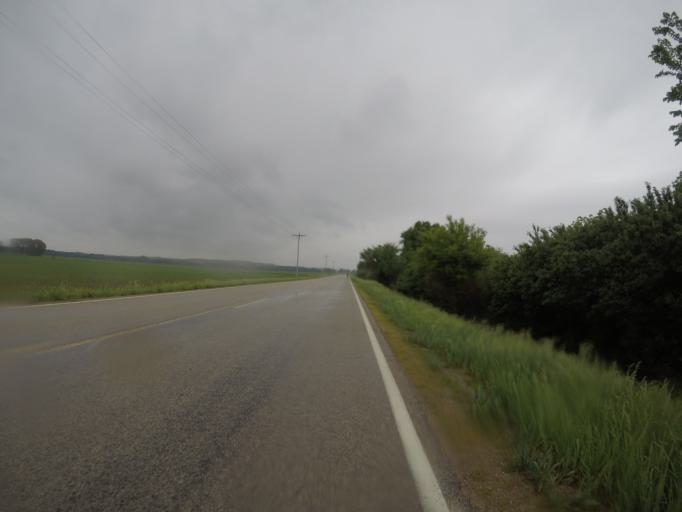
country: US
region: Kansas
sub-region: Pottawatomie County
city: Wamego
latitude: 39.3060
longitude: -96.2308
